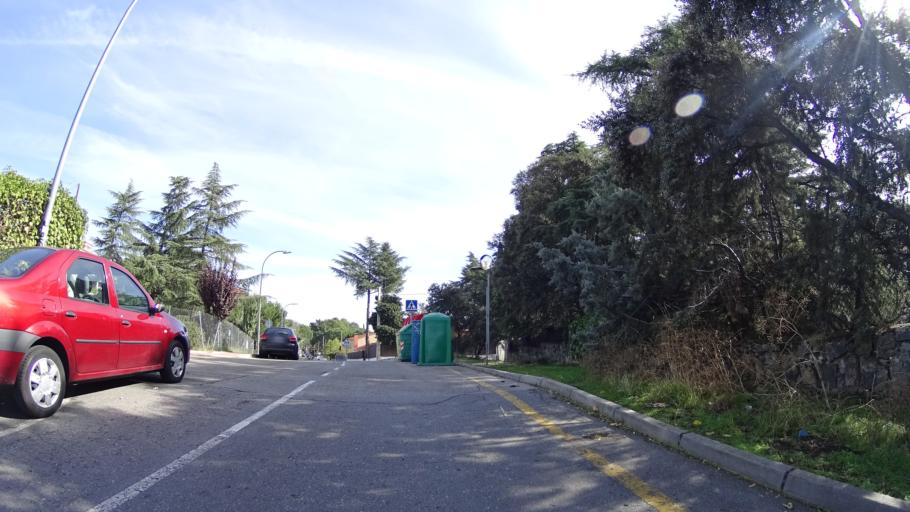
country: ES
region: Madrid
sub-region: Provincia de Madrid
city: Collado-Villalba
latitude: 40.6169
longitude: -4.0122
